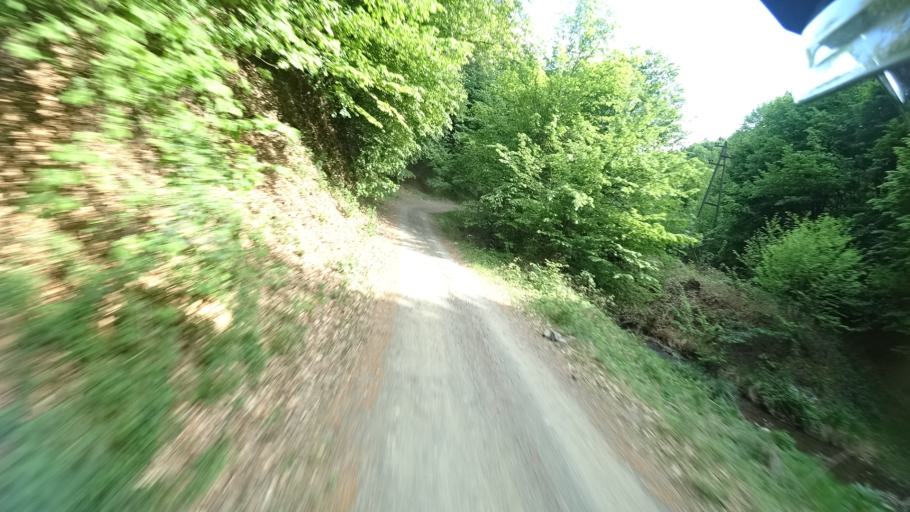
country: HR
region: Grad Zagreb
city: Kasina
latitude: 45.9292
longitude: 15.9524
